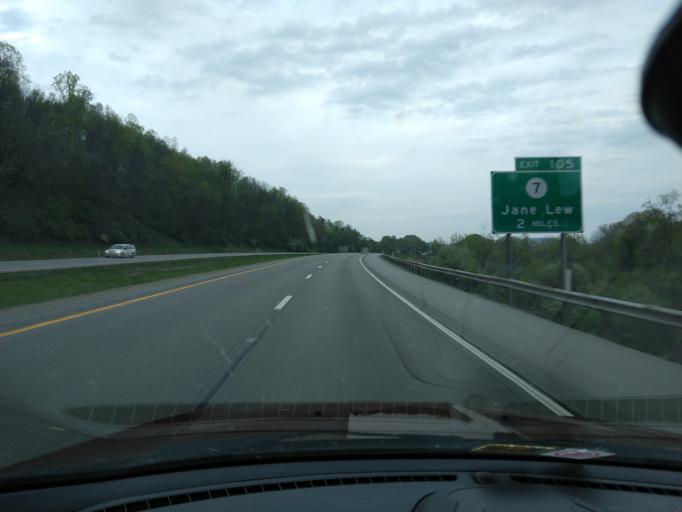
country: US
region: West Virginia
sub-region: Lewis County
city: Weston
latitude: 39.0737
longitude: -80.4050
